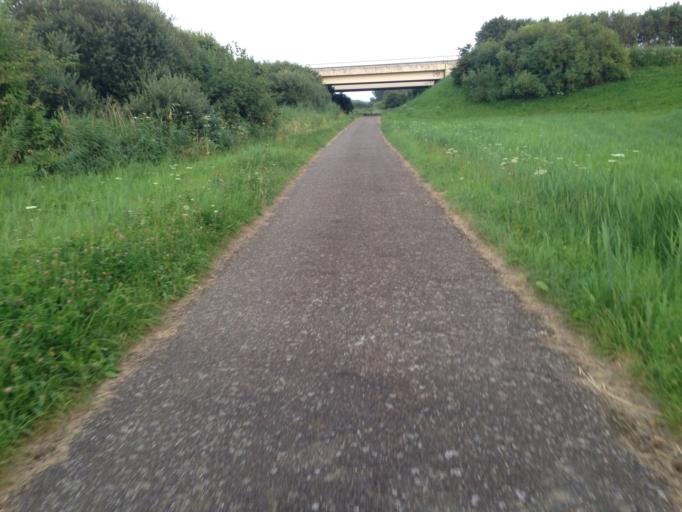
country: NL
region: Flevoland
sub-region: Gemeente Almere
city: Almere Stad
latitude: 52.3985
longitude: 5.2443
